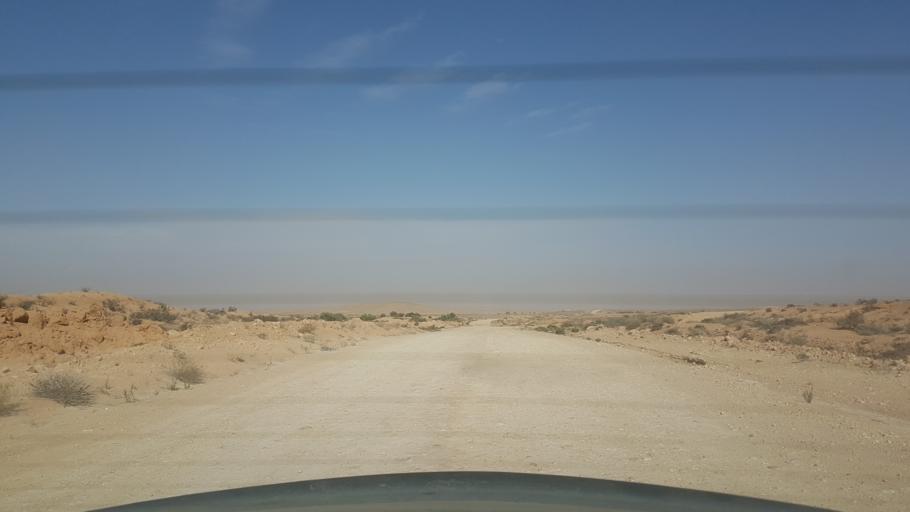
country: TN
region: Qabis
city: El Hamma
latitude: 33.6609
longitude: 9.7347
